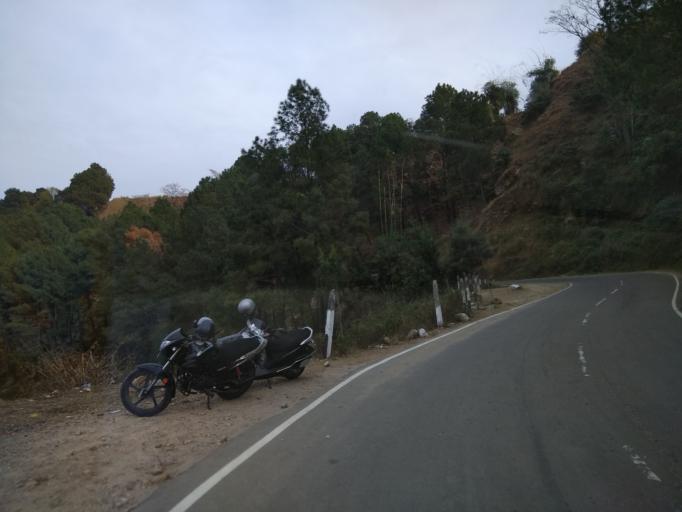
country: IN
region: Himachal Pradesh
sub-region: Kangra
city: Palampur
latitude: 32.1096
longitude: 76.4876
